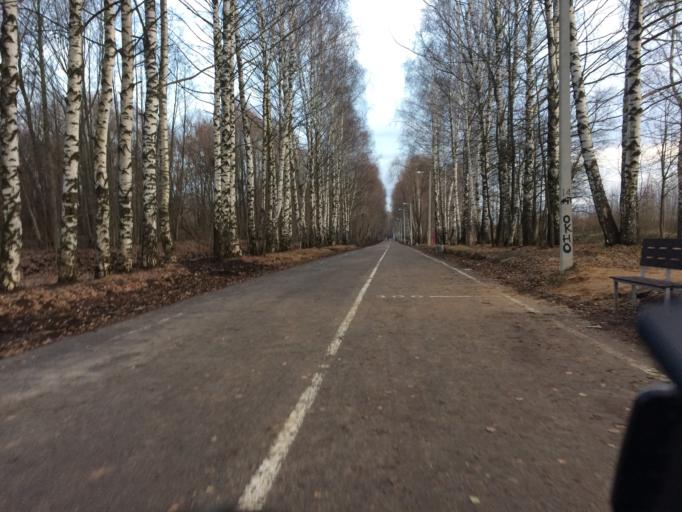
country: RU
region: Mariy-El
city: Yoshkar-Ola
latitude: 56.6252
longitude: 47.9090
